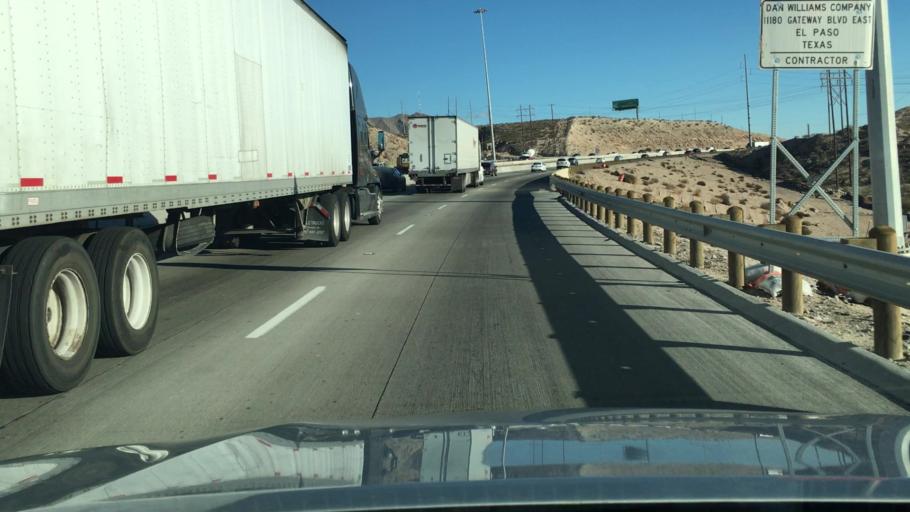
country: US
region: New Mexico
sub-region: Dona Ana County
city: Sunland Park
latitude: 31.8087
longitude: -106.5262
